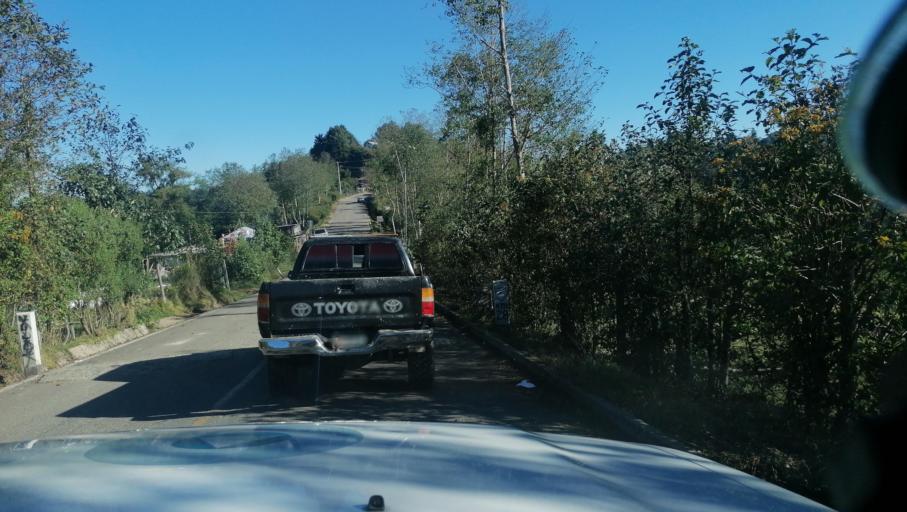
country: MX
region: Chiapas
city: Motozintla de Mendoza
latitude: 15.2438
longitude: -92.2290
